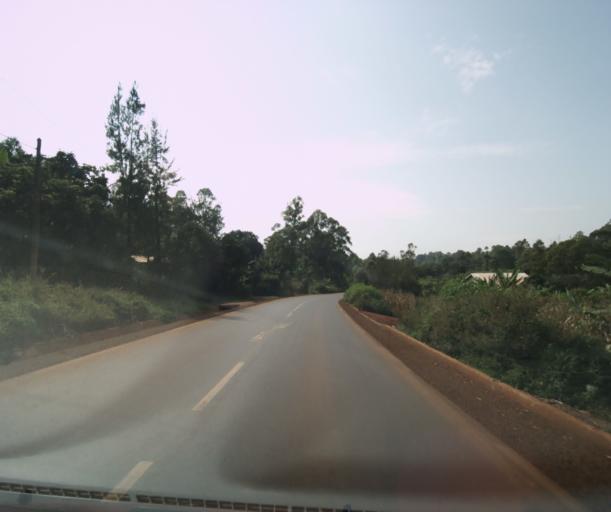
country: CM
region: West
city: Mbouda
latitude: 5.6182
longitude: 10.2841
